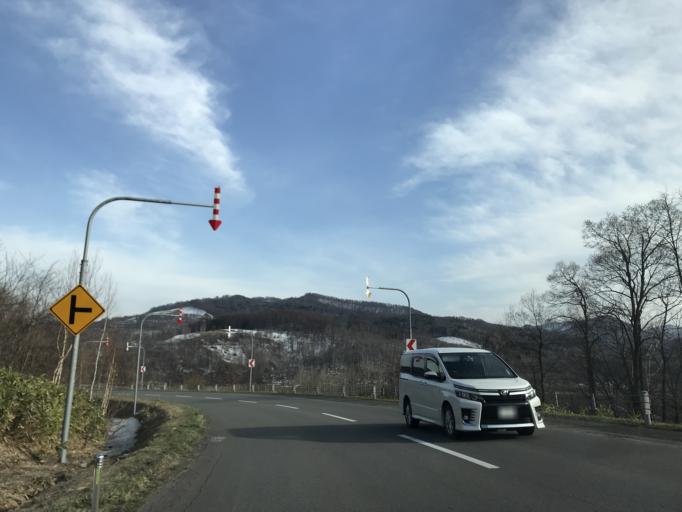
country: JP
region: Hokkaido
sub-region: Asahikawa-shi
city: Asahikawa
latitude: 43.6956
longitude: 142.3307
